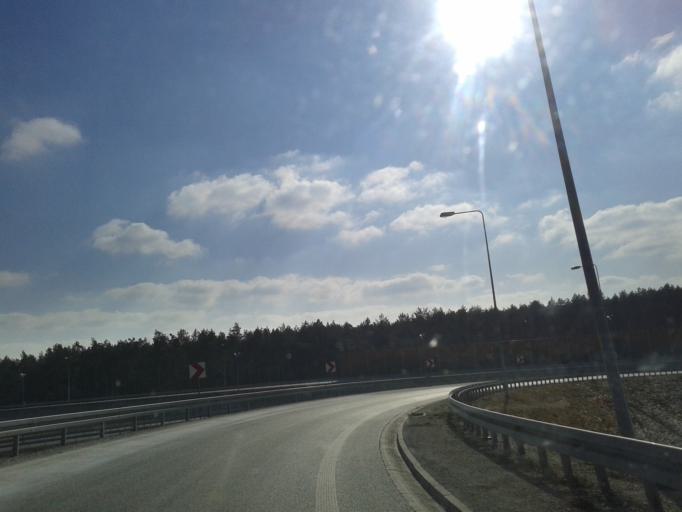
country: PL
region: Kujawsko-Pomorskie
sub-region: Powiat aleksandrowski
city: Ciechocinek
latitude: 52.8669
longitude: 18.7587
